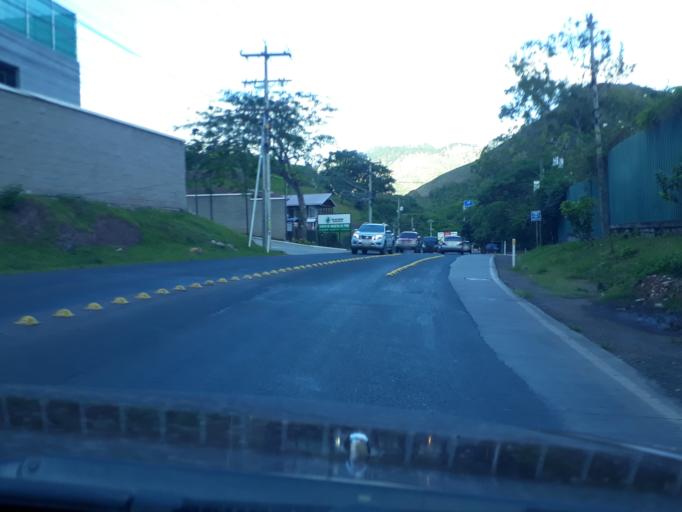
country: HN
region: Francisco Morazan
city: Tegucigalpa
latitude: 14.1108
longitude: -87.1666
